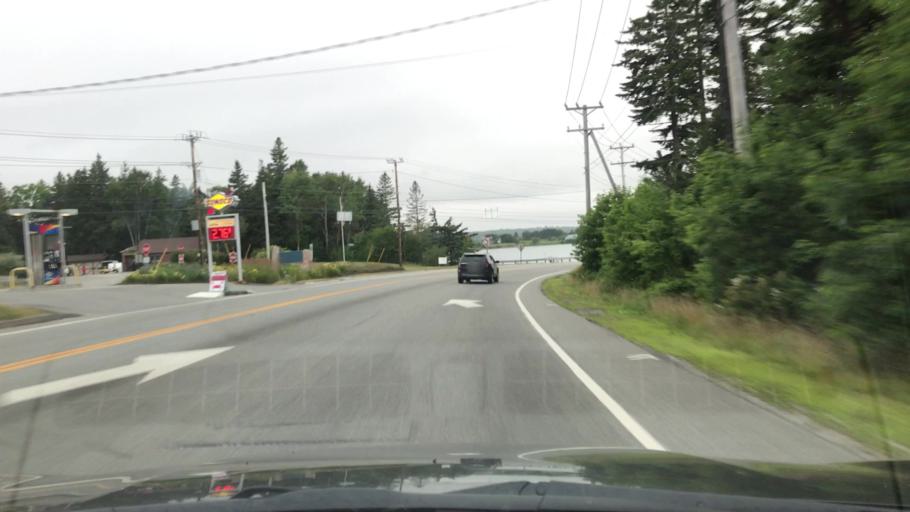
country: US
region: Maine
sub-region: Hancock County
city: Trenton
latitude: 44.4213
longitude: -68.3627
